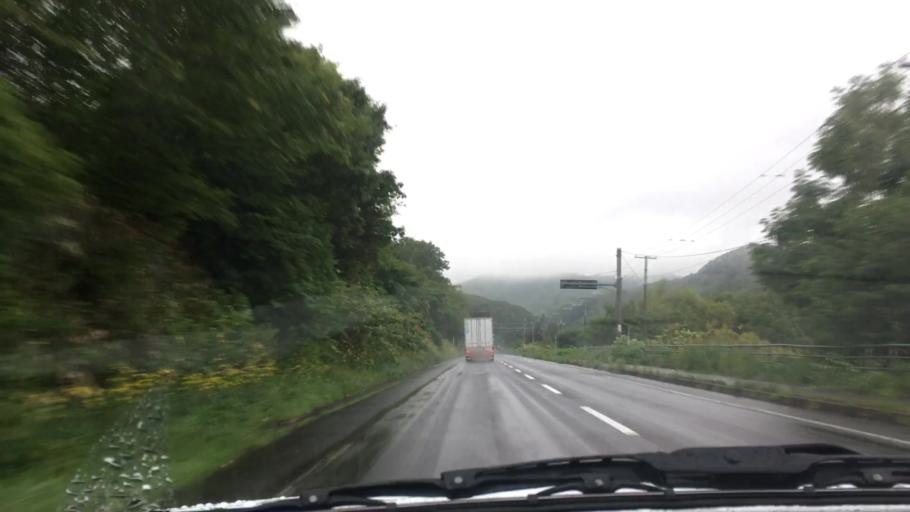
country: JP
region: Hokkaido
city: Niseko Town
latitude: 42.6000
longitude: 140.6291
